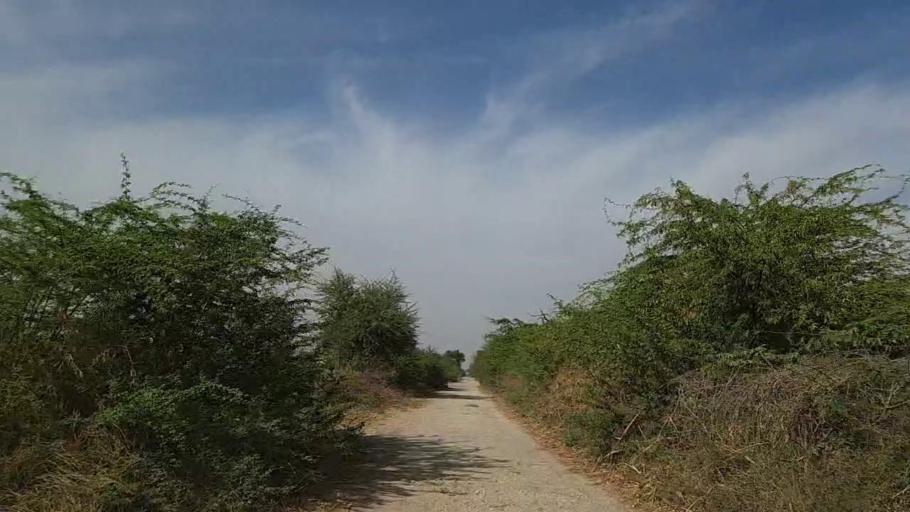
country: PK
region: Sindh
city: Samaro
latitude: 25.2371
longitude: 69.4239
